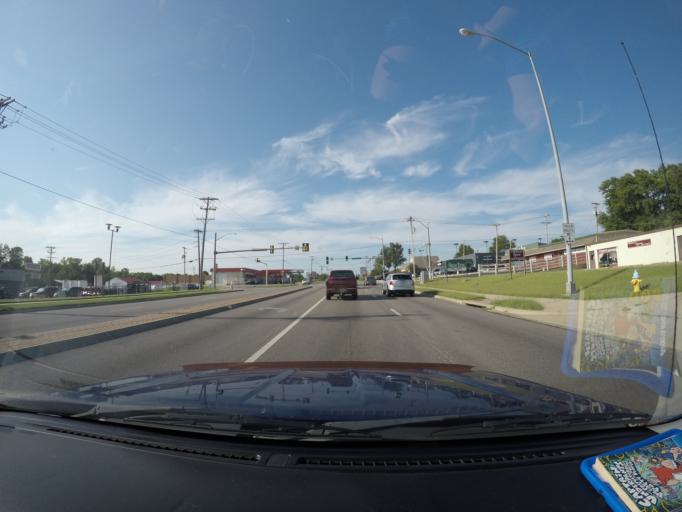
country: US
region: Kansas
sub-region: Leavenworth County
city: Lansing
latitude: 39.2665
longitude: -94.8998
